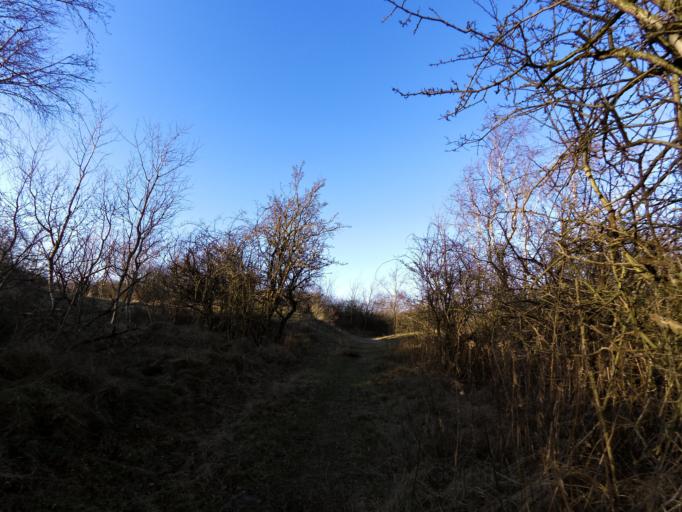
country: NL
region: South Holland
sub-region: Gemeente Goeree-Overflakkee
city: Goedereede
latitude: 51.8896
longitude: 4.0397
